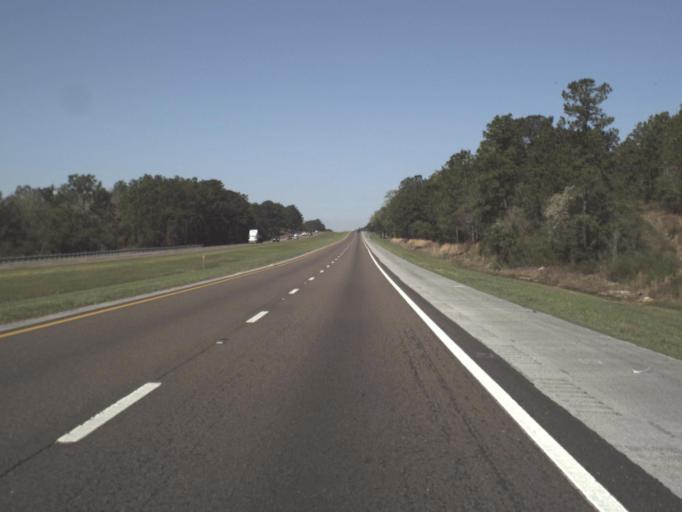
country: US
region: Florida
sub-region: Walton County
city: DeFuniak Springs
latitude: 30.7228
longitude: -86.1897
